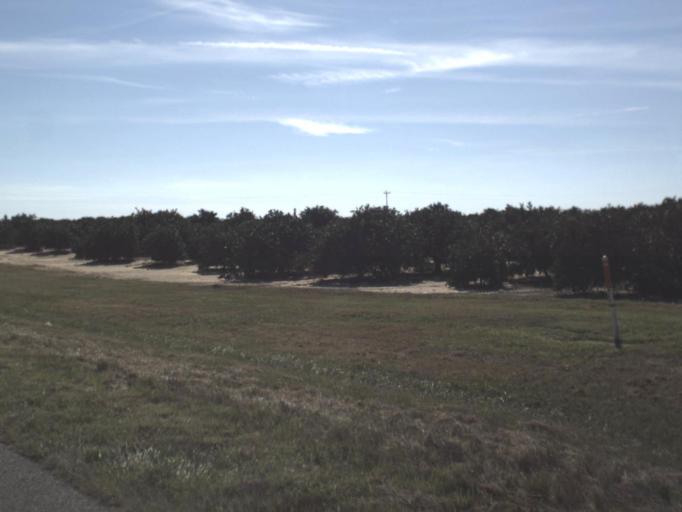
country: US
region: Florida
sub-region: Highlands County
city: Placid Lakes
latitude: 27.1550
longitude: -81.3289
